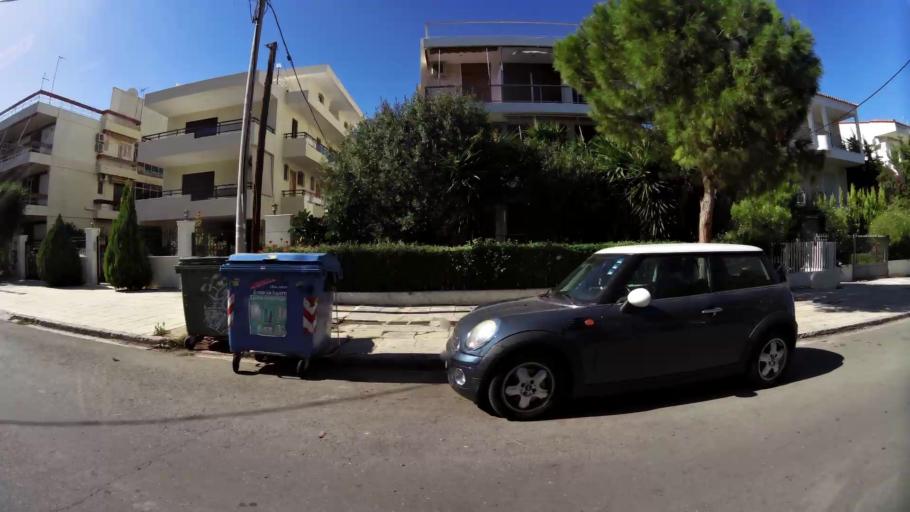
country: GR
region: Attica
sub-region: Nomarchia Anatolikis Attikis
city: Vouliagmeni
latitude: 37.8154
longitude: 23.7821
